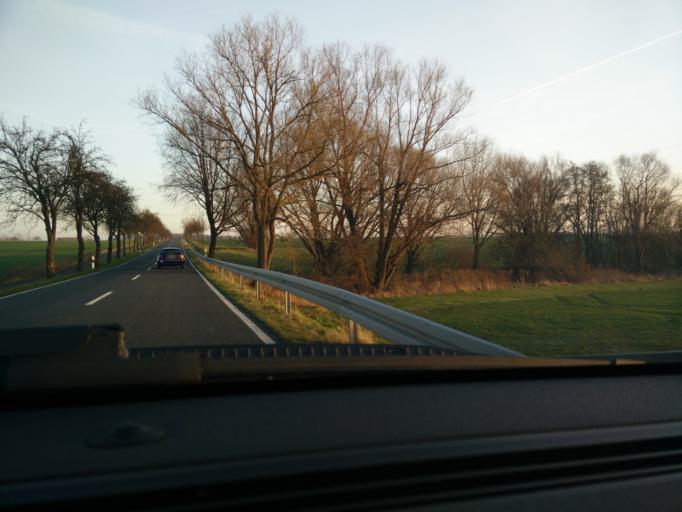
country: DE
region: Saxony
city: Kitzscher
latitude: 51.1675
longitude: 12.5341
